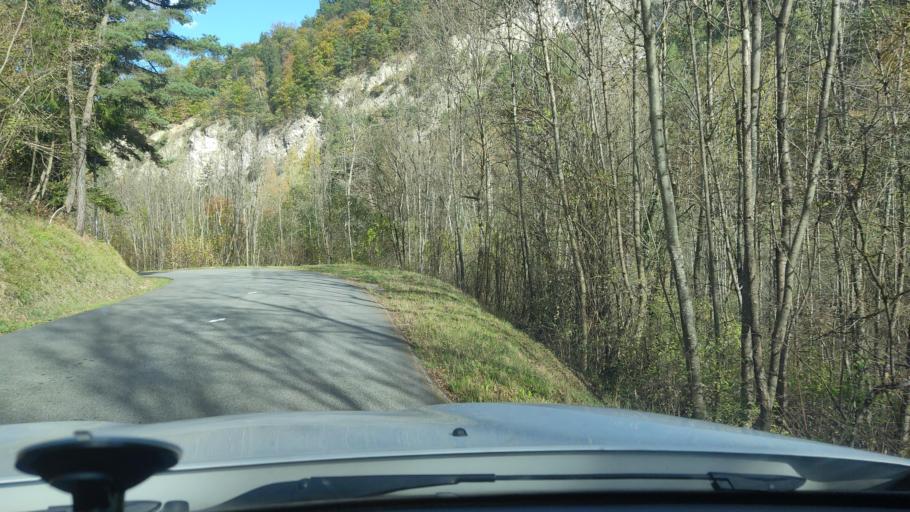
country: FR
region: Rhone-Alpes
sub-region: Departement de la Savoie
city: Saint-Jean-de-Maurienne
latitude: 45.2448
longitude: 6.3212
